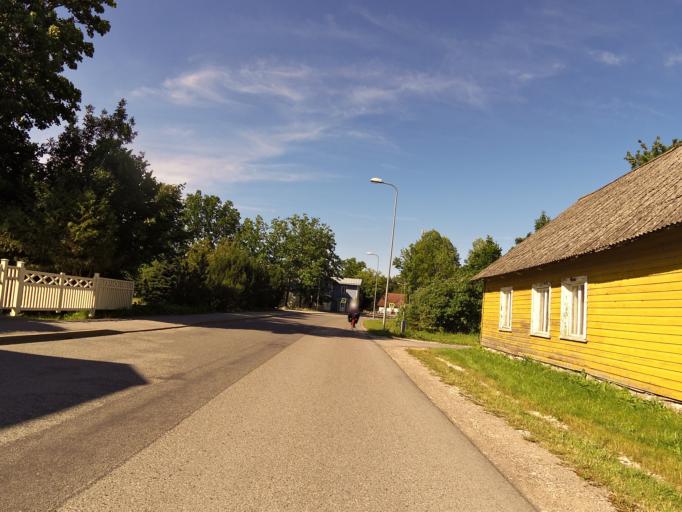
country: EE
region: Hiiumaa
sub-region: Kaerdla linn
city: Kardla
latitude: 59.0001
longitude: 22.7464
